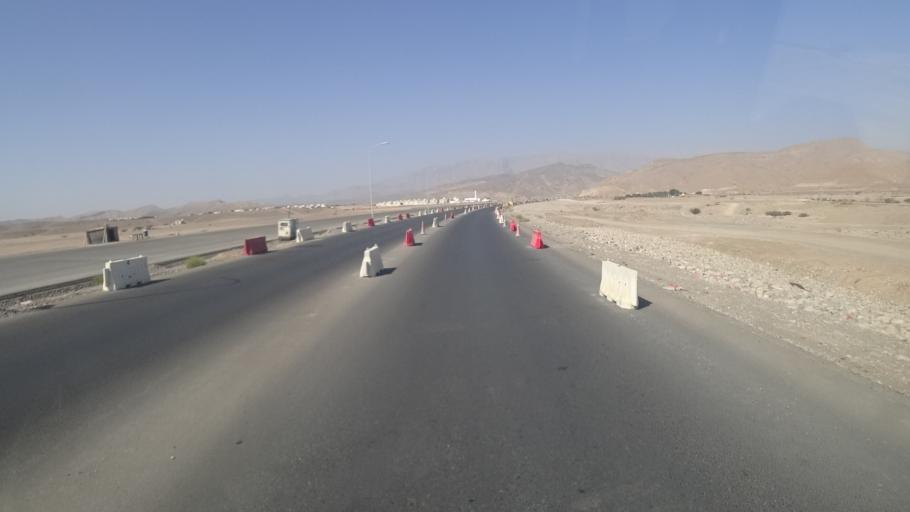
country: OM
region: Ash Sharqiyah
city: Sur
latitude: 22.5173
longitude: 59.4546
